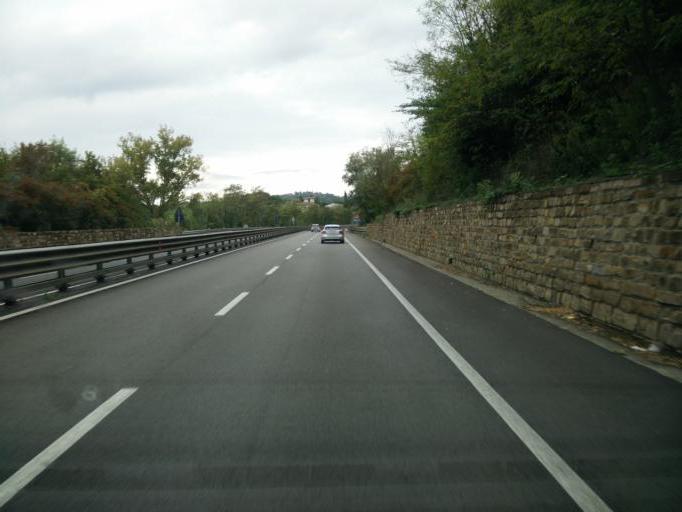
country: IT
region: Tuscany
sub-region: Provincia di Siena
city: Poggibonsi
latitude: 43.4779
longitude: 11.1509
